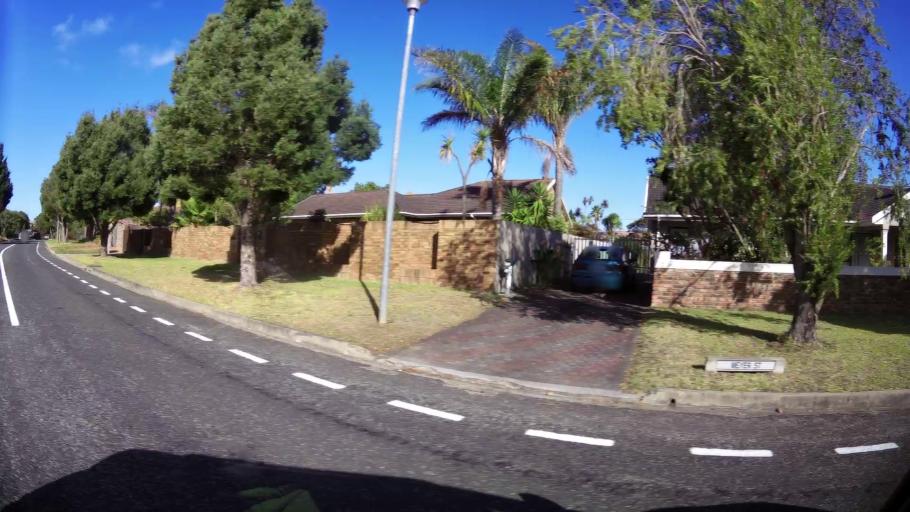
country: ZA
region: Western Cape
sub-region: Eden District Municipality
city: George
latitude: -33.9645
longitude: 22.4932
